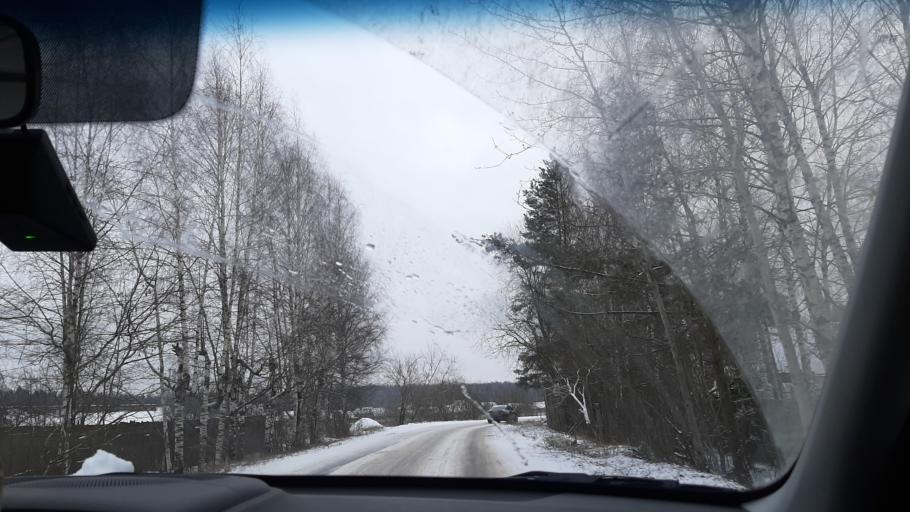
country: RU
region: Ivanovo
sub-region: Gorod Ivanovo
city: Ivanovo
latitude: 56.9330
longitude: 40.9734
